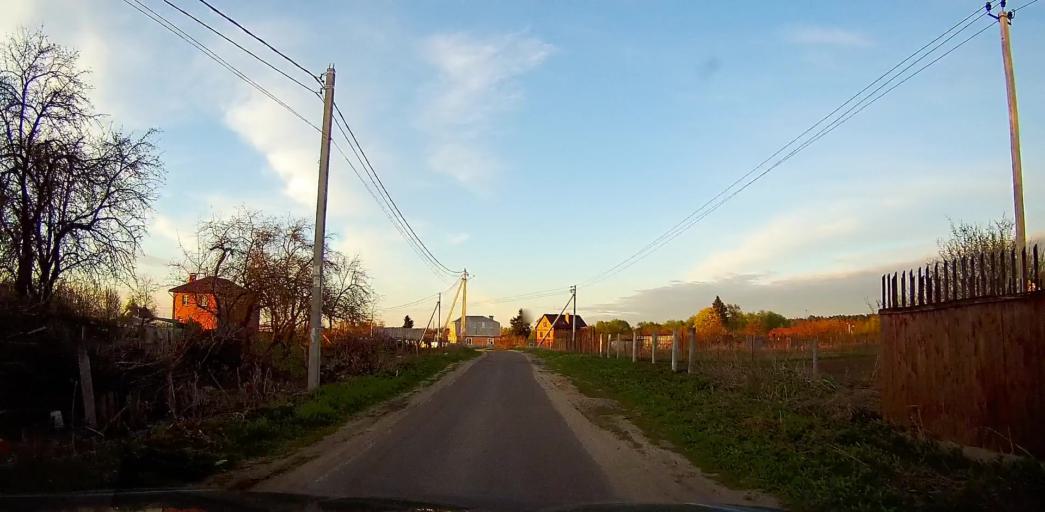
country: RU
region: Moskovskaya
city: Peski
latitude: 55.2099
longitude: 38.7397
